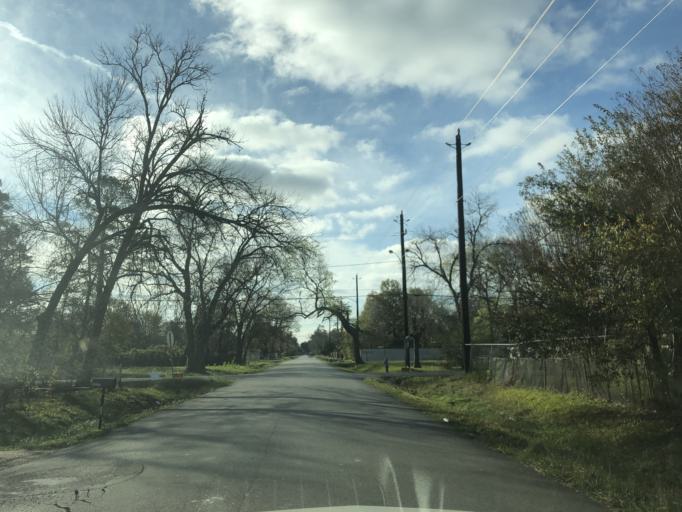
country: US
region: Texas
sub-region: Harris County
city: Jacinto City
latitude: 29.8363
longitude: -95.2938
